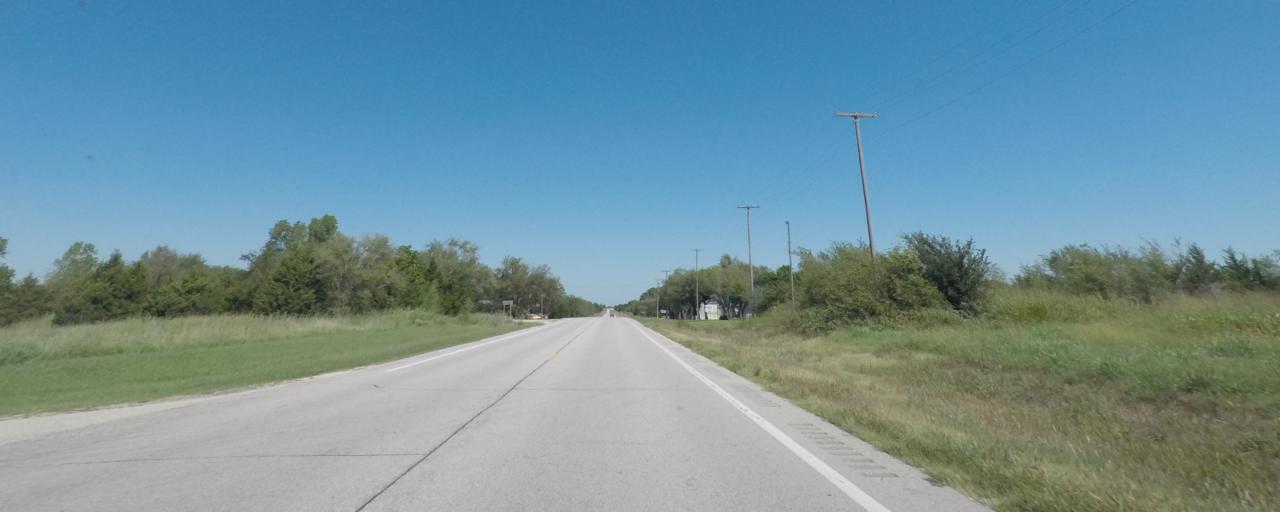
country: US
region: Kansas
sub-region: Sumner County
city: Wellington
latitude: 37.3706
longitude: -97.3850
